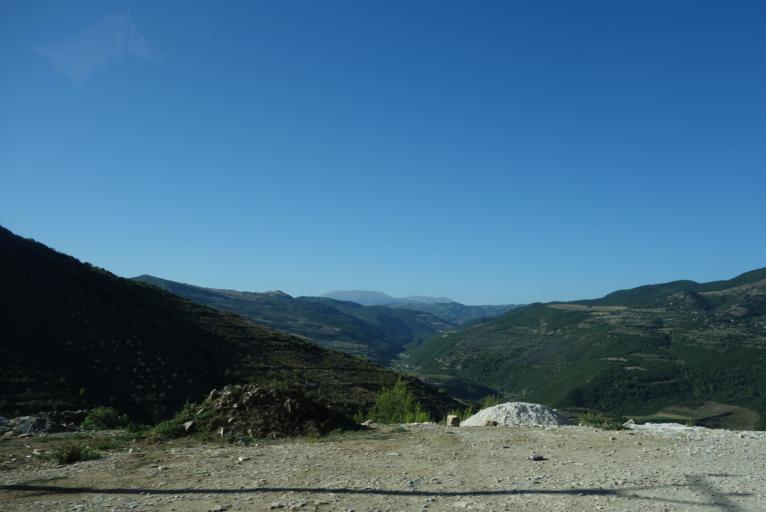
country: AL
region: Berat
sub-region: Rrethi i Beratit
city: Polican
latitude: 40.6054
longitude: 20.1041
